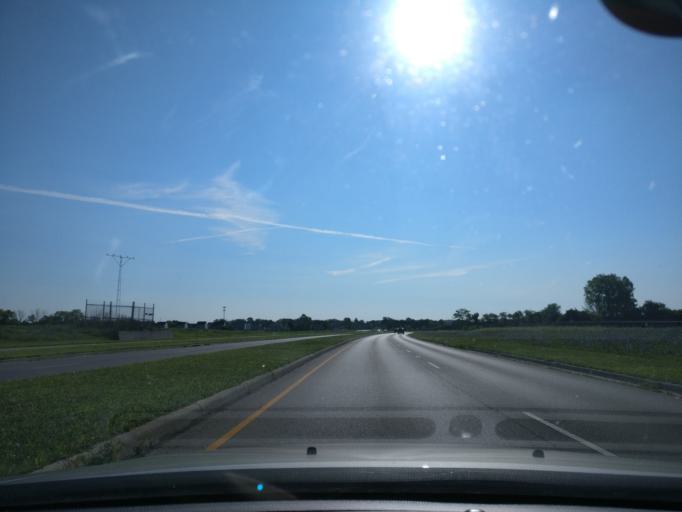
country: US
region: Ohio
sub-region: Warren County
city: Five Points
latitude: 39.5971
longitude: -84.2211
